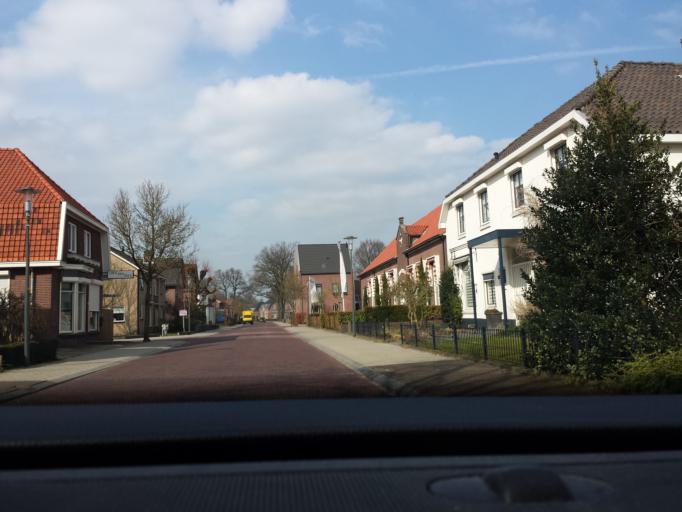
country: NL
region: Gelderland
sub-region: Oost Gelre
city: Lichtenvoorde
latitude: 52.0044
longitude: 6.5196
